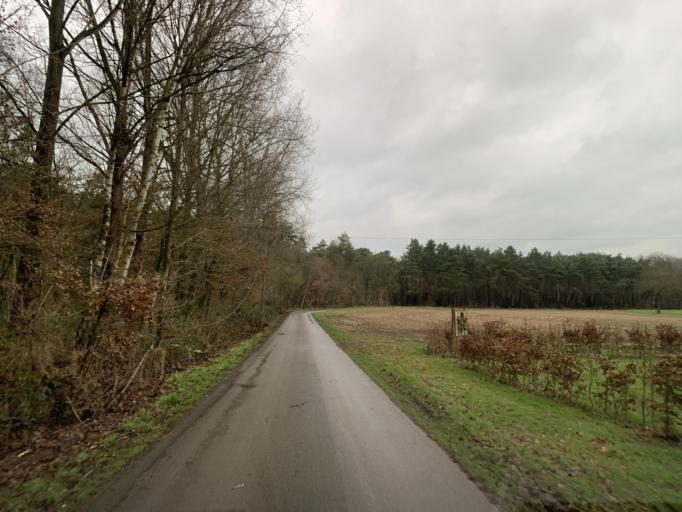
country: DE
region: North Rhine-Westphalia
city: Olfen
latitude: 51.7684
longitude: 7.3349
